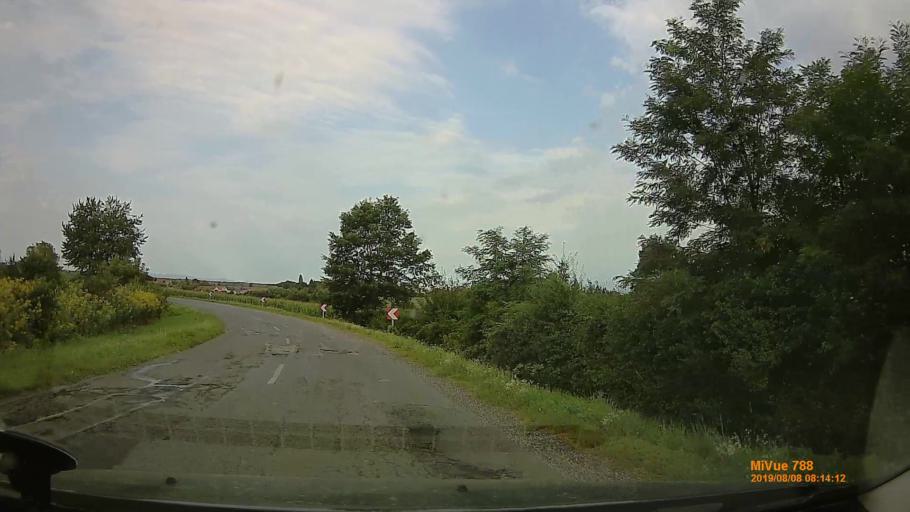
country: HU
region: Zala
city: Murakeresztur
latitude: 46.4005
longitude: 16.8561
